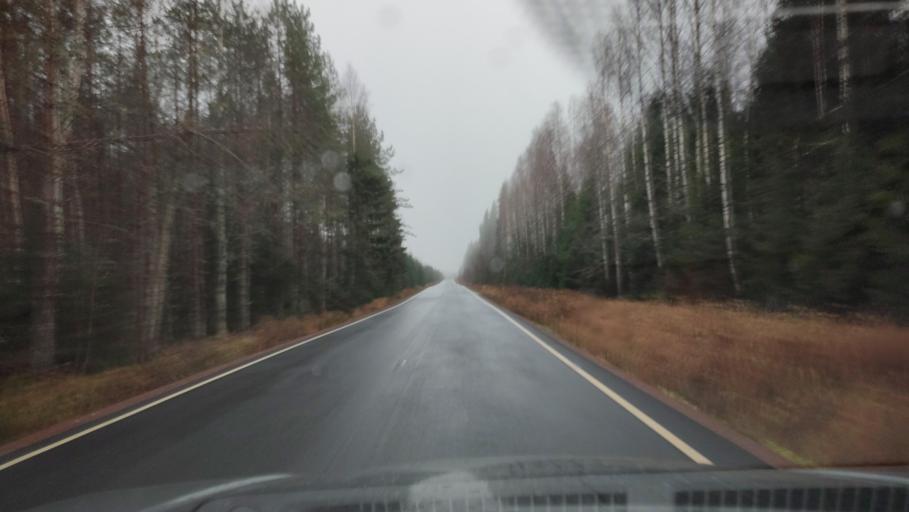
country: FI
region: Southern Ostrobothnia
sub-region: Suupohja
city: Karijoki
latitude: 62.1548
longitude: 21.7137
